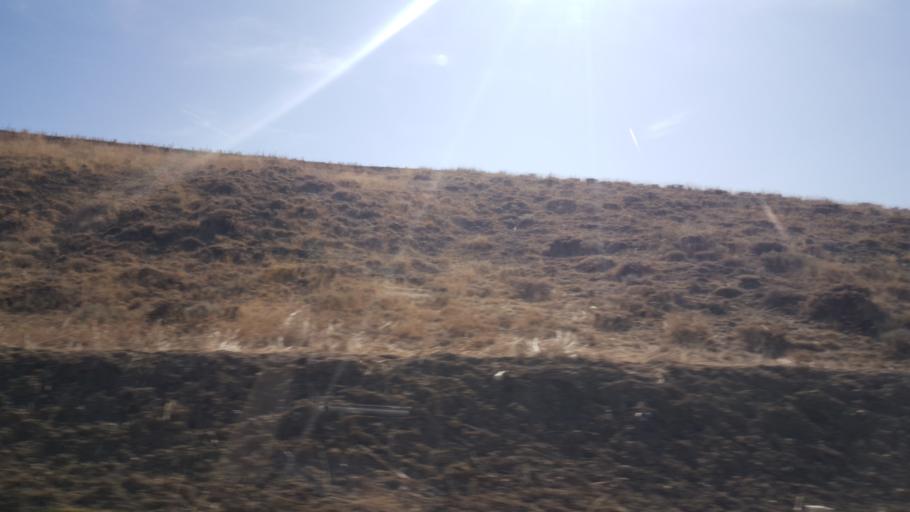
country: TR
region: Ankara
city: Yenice
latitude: 39.2909
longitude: 32.6338
